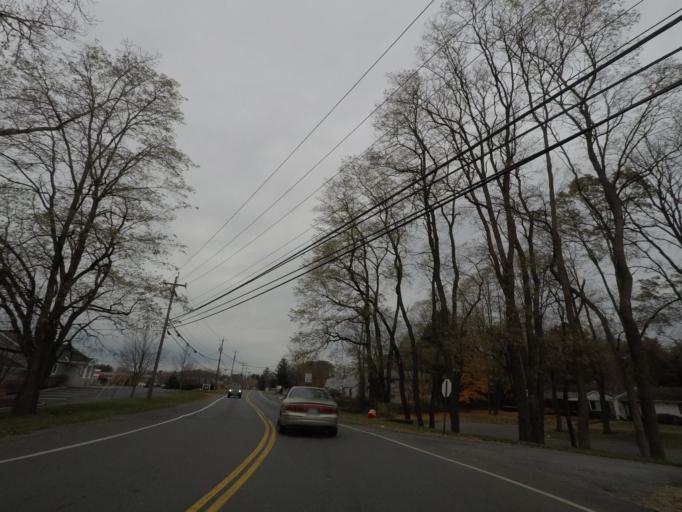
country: US
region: New York
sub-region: Saratoga County
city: Country Knolls
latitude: 42.8641
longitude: -73.7655
